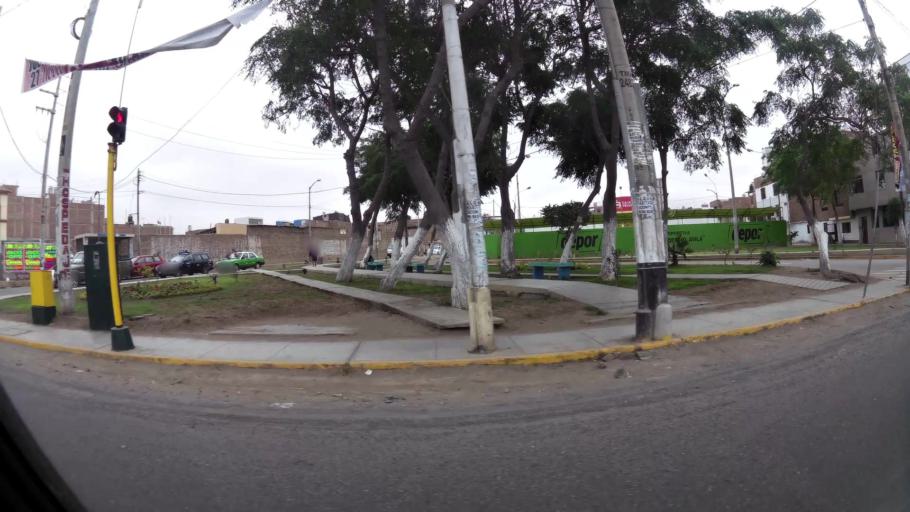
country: PE
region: La Libertad
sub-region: Provincia de Trujillo
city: La Esperanza
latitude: -8.1007
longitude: -79.0504
